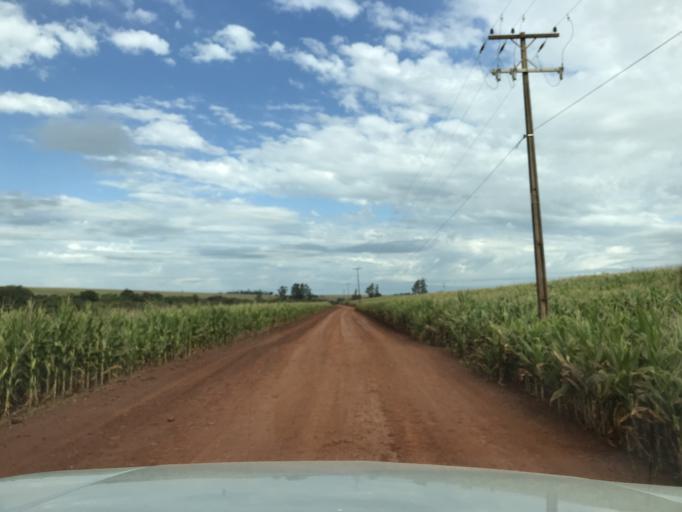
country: BR
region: Parana
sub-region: Palotina
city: Palotina
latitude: -24.3160
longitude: -53.8070
